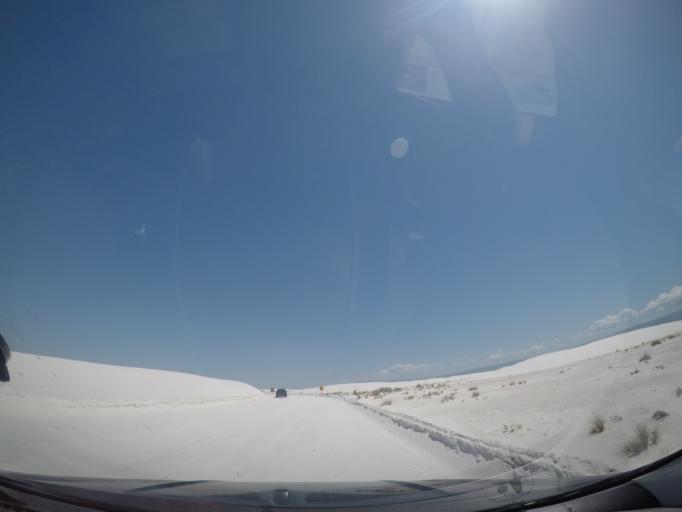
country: US
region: New Mexico
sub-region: Otero County
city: Holloman Air Force Base
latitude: 32.8090
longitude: -106.2619
